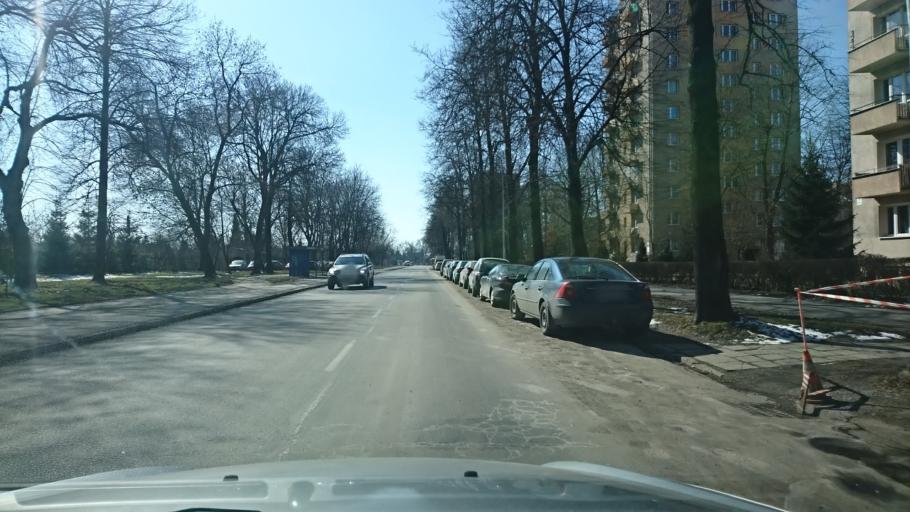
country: PL
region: Lesser Poland Voivodeship
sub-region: Powiat wielicki
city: Kokotow
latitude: 50.0716
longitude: 20.0535
